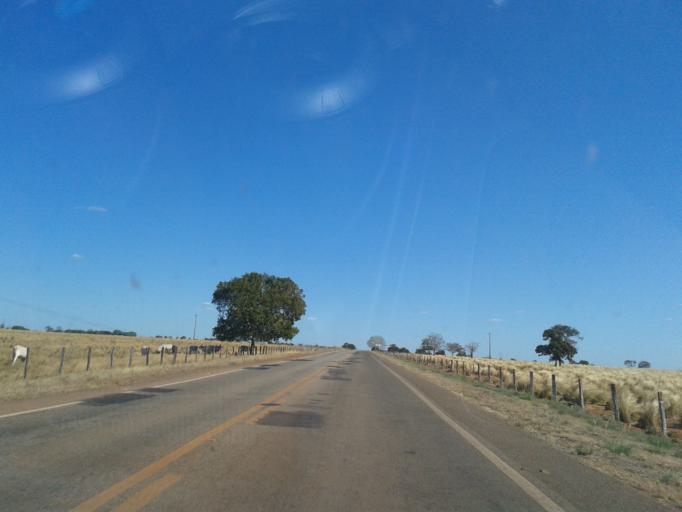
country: BR
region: Goias
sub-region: Crixas
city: Crixas
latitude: -14.1435
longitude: -50.3575
